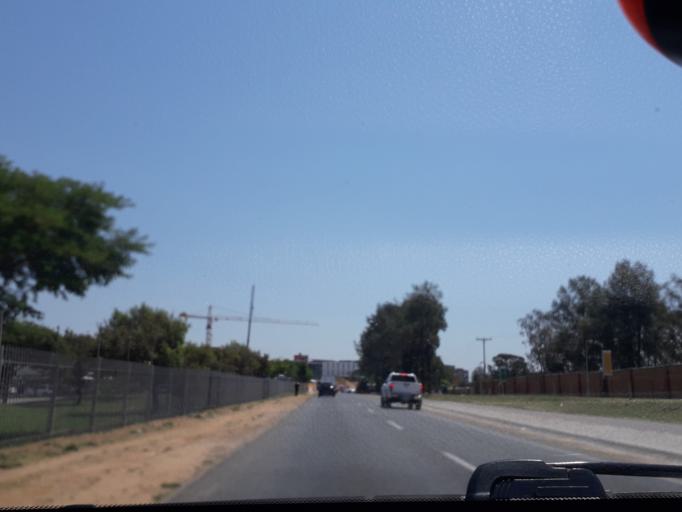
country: ZA
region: Gauteng
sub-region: City of Johannesburg Metropolitan Municipality
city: Midrand
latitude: -26.0429
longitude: 28.0967
